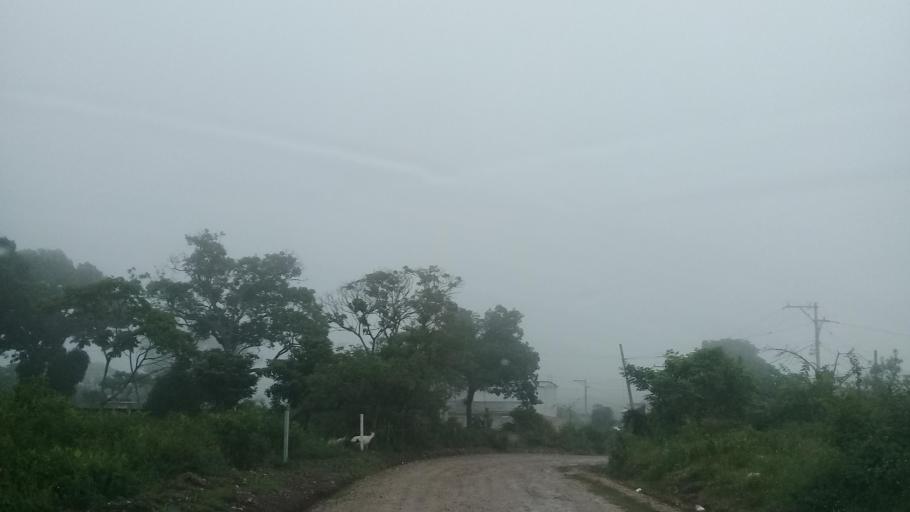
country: MX
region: Veracruz
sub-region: Xalapa
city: Fraccionamiento las Fuentes
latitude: 19.4931
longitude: -96.8815
